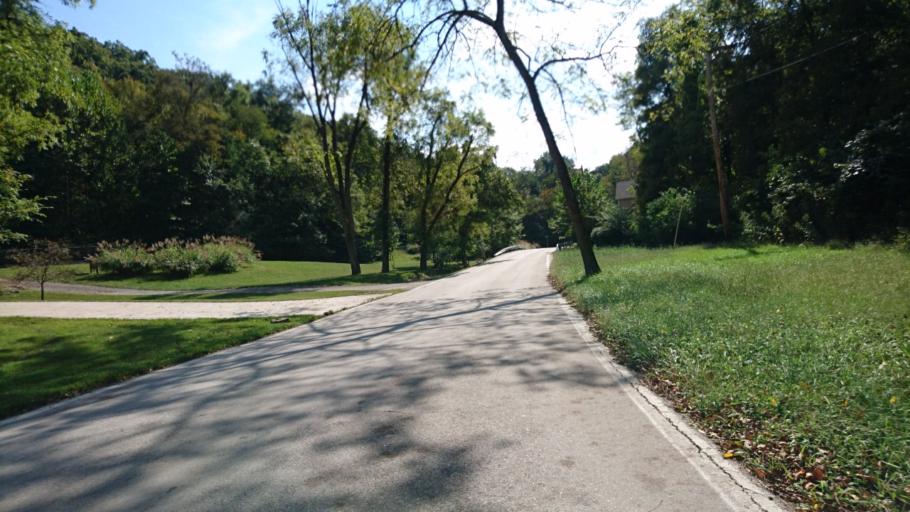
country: US
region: Missouri
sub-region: Saint Louis County
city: Wildwood
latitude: 38.5648
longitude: -90.6365
